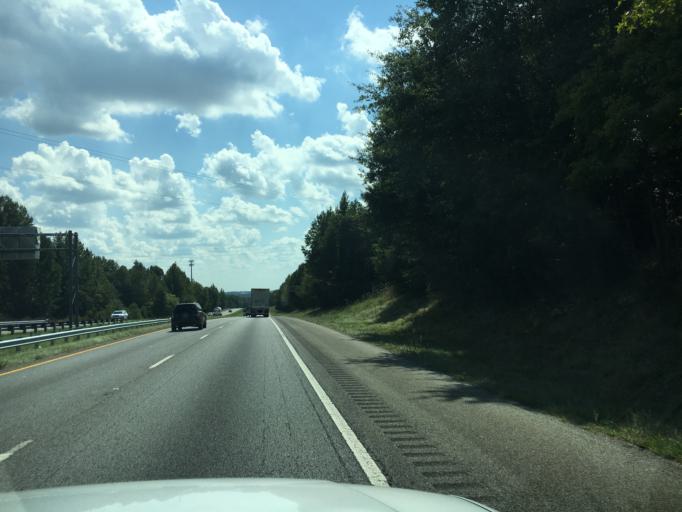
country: US
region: South Carolina
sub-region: Spartanburg County
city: Roebuck
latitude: 34.8966
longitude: -81.9924
